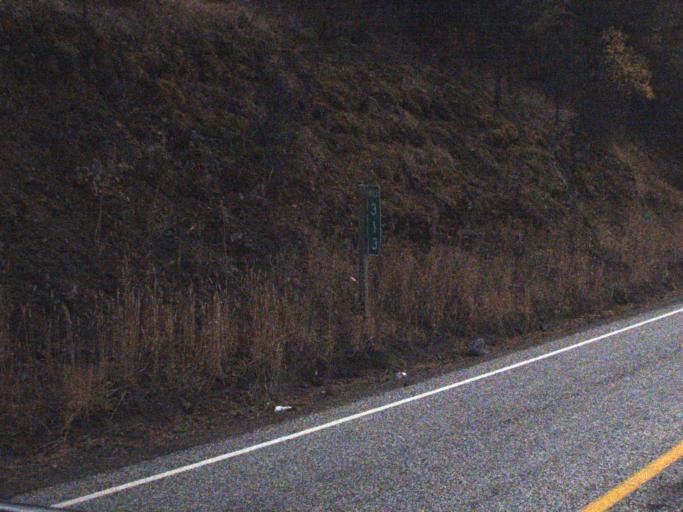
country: US
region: Washington
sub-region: Ferry County
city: Republic
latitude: 48.6133
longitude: -118.5785
